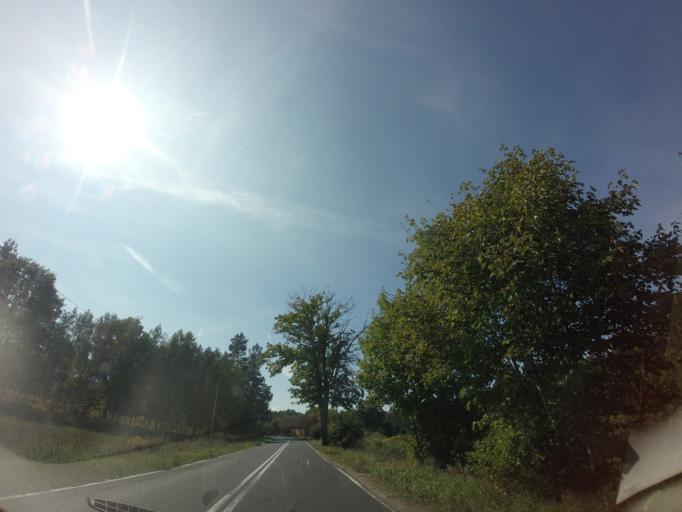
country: PL
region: Lubusz
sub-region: Powiat strzelecko-drezdenecki
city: Stare Kurowo
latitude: 52.7628
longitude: 15.6965
